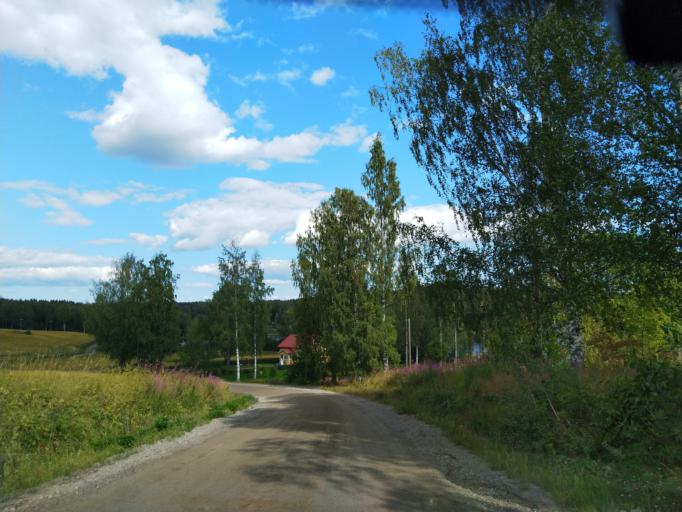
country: FI
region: Pirkanmaa
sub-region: Ylae-Pirkanmaa
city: Ruovesi
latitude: 61.9594
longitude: 24.0339
